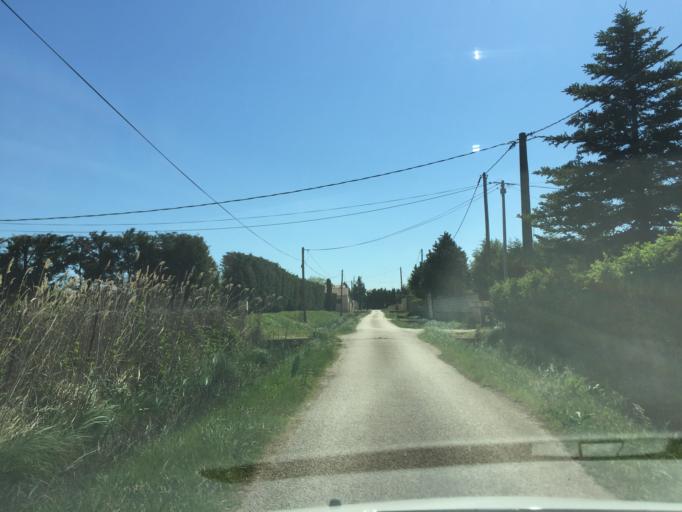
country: FR
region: Provence-Alpes-Cote d'Azur
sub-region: Departement du Vaucluse
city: Courthezon
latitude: 44.0889
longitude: 4.8686
